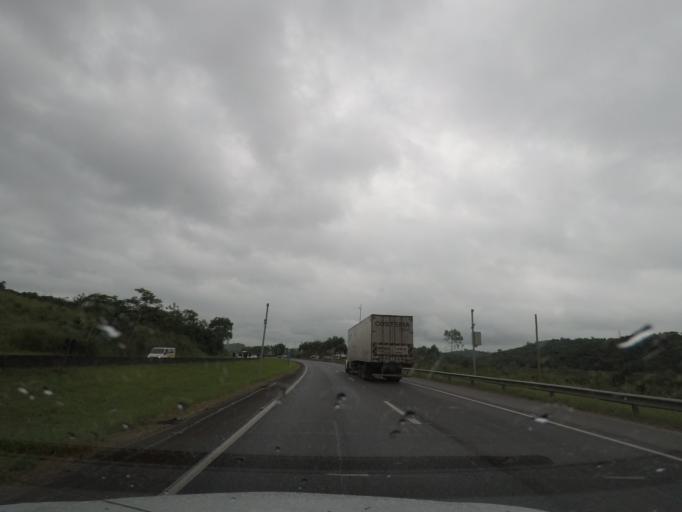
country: BR
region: Sao Paulo
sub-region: Registro
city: Registro
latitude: -24.4223
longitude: -47.7772
